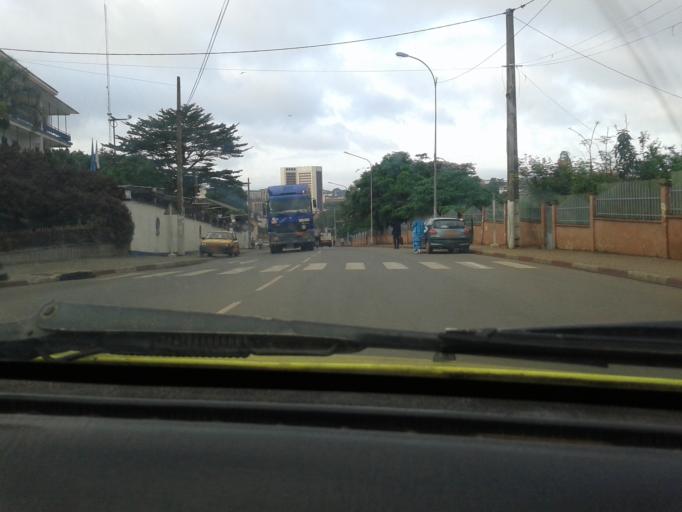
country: CM
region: Centre
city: Yaounde
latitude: 3.8751
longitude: 11.5150
